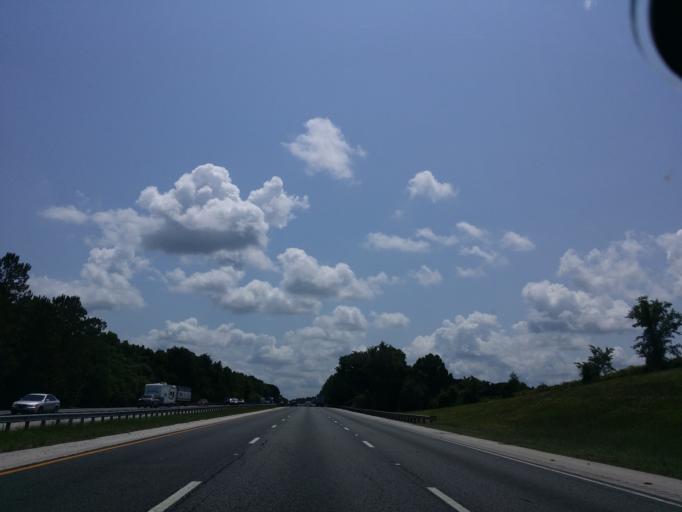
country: US
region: Florida
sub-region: Marion County
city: Citra
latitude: 29.4400
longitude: -82.2656
